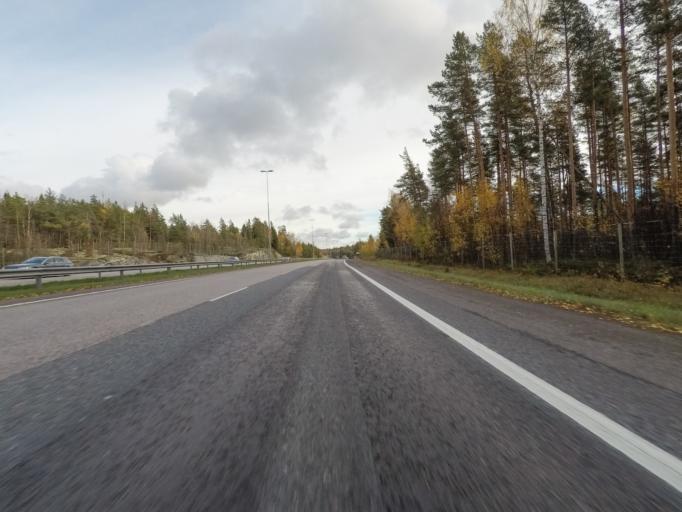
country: FI
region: Uusimaa
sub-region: Helsinki
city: Sibbo
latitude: 60.2748
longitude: 25.2478
